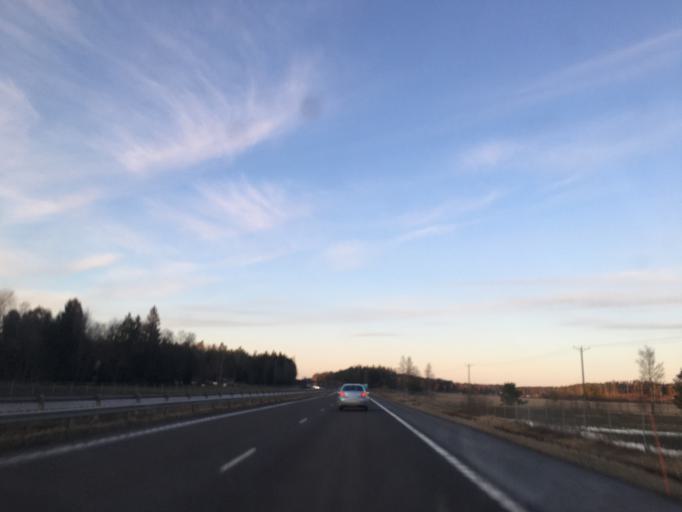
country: FI
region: Varsinais-Suomi
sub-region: Turku
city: Turku
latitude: 60.5201
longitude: 22.3043
